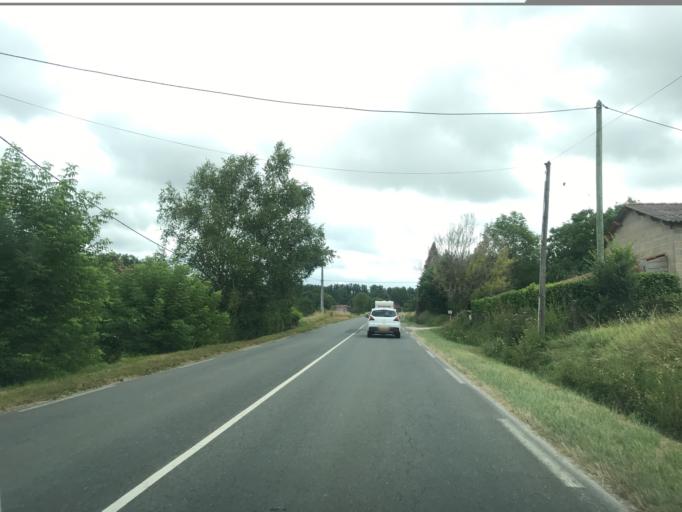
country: FR
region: Aquitaine
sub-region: Departement de la Dordogne
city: Mareuil
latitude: 45.4457
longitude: 0.4692
